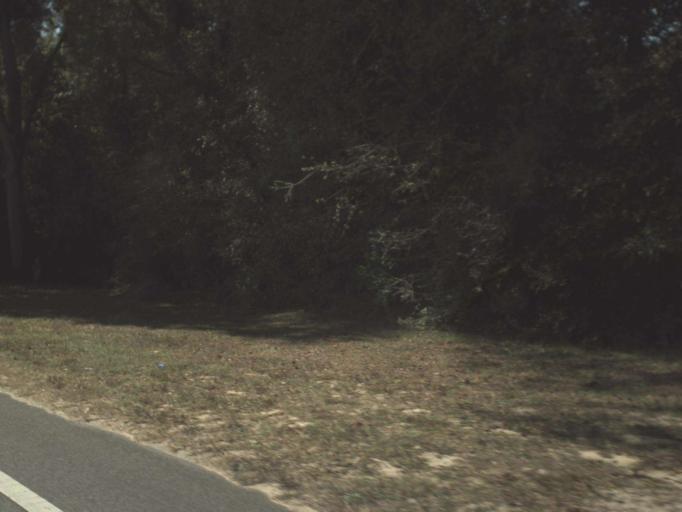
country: US
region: Florida
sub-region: Walton County
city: DeFuniak Springs
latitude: 30.7325
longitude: -86.1145
